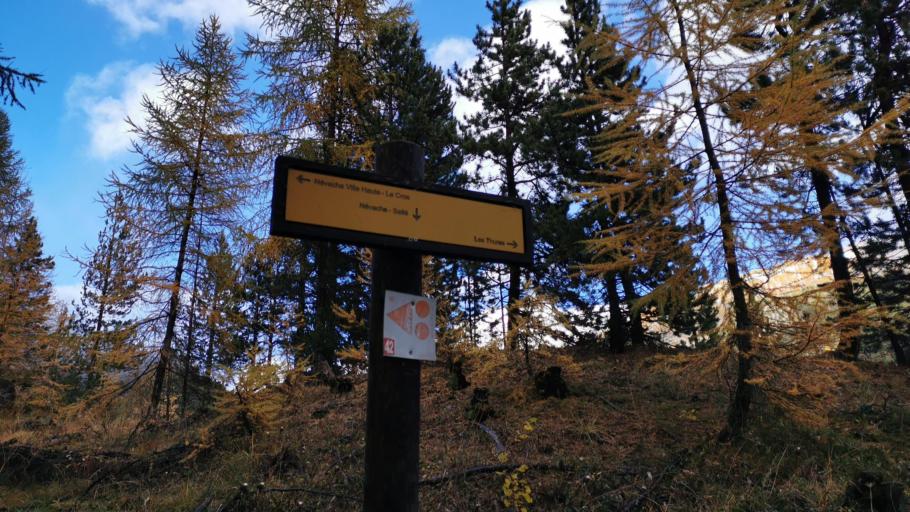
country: IT
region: Piedmont
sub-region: Provincia di Torino
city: Bardonecchia
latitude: 45.0304
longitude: 6.6299
